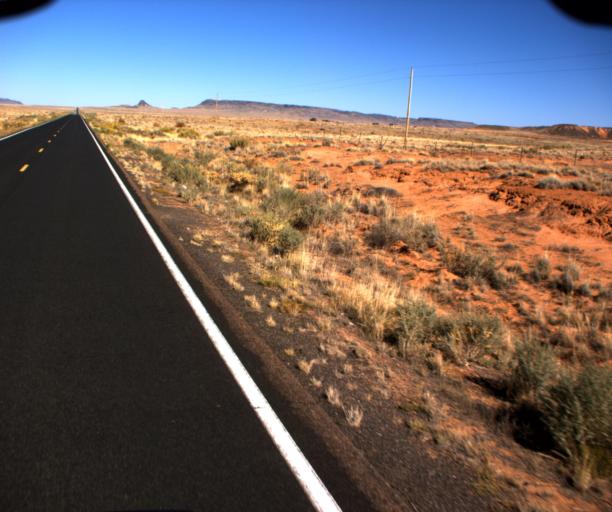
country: US
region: Arizona
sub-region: Navajo County
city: Dilkon
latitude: 35.3345
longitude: -110.4236
